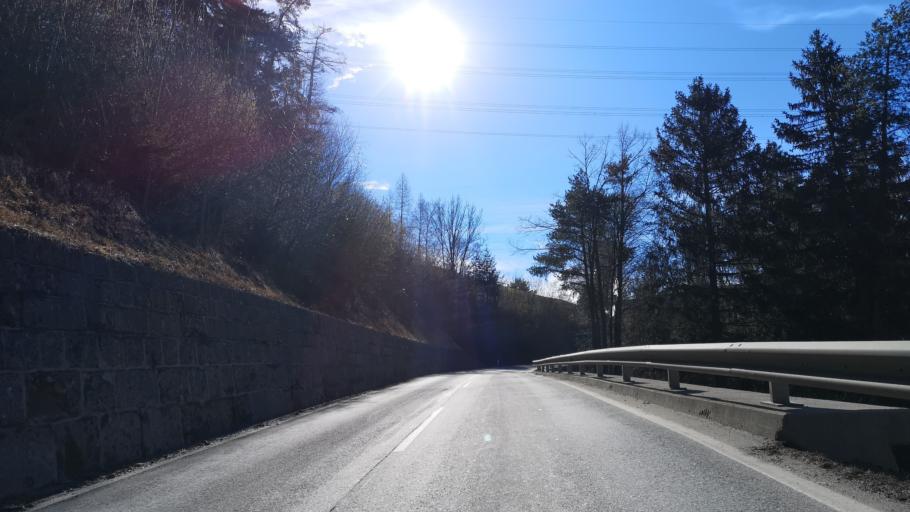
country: AT
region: Tyrol
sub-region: Politischer Bezirk Innsbruck Land
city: Mutters
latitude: 47.2404
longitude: 11.3999
